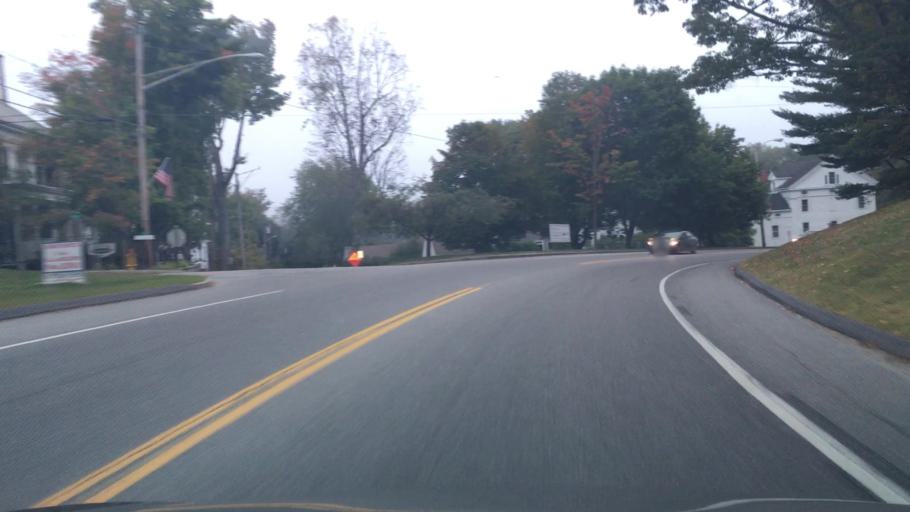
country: US
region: Maine
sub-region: Lincoln County
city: Wiscasset
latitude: 44.0047
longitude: -69.6677
